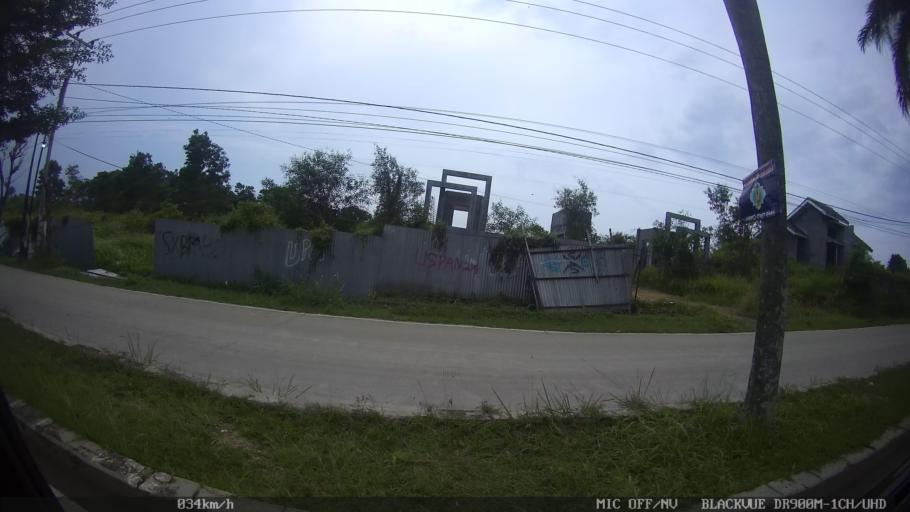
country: ID
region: Lampung
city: Kedaton
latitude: -5.3783
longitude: 105.2119
